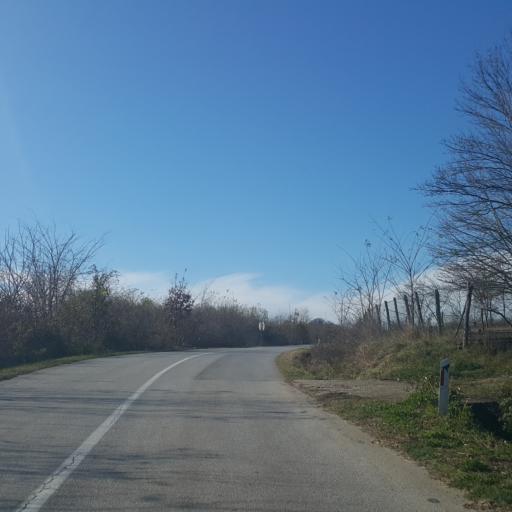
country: RS
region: Central Serbia
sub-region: Sumadijski Okrug
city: Raca
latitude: 44.2410
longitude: 20.8764
